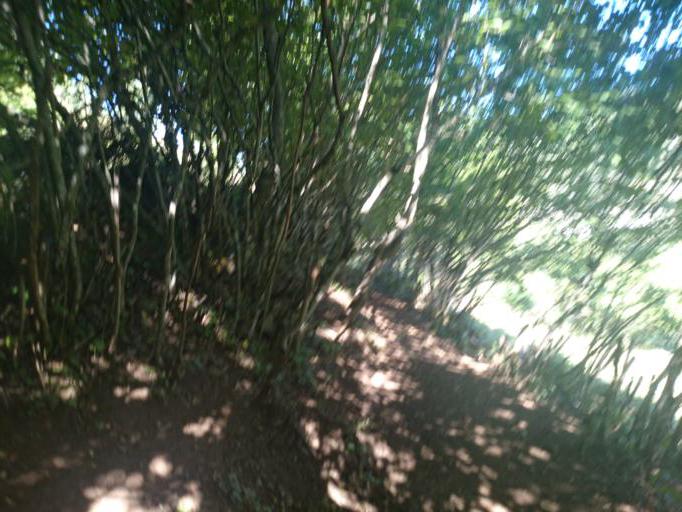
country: AL
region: Diber
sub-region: Rrethi i Bulqizes
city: Martanesh
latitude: 41.4009
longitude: 20.1712
